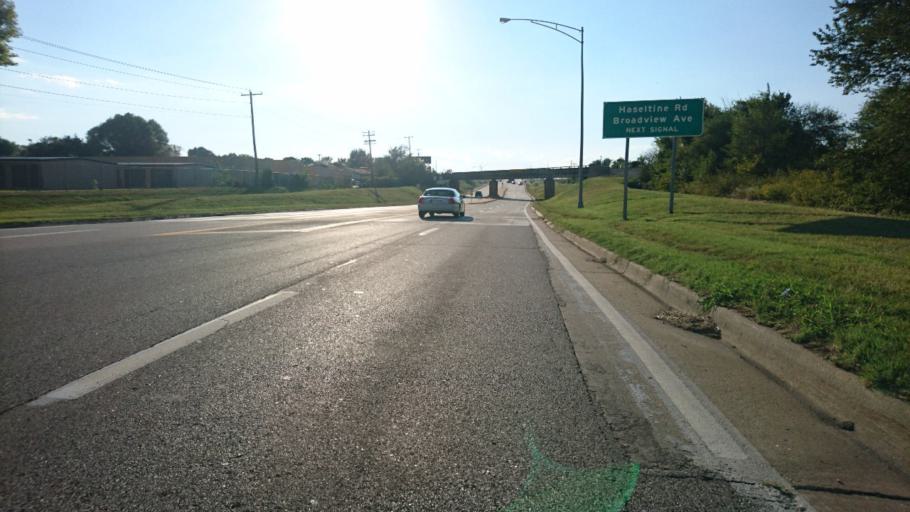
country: US
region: Missouri
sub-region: Greene County
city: Springfield
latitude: 37.2126
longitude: -93.3767
